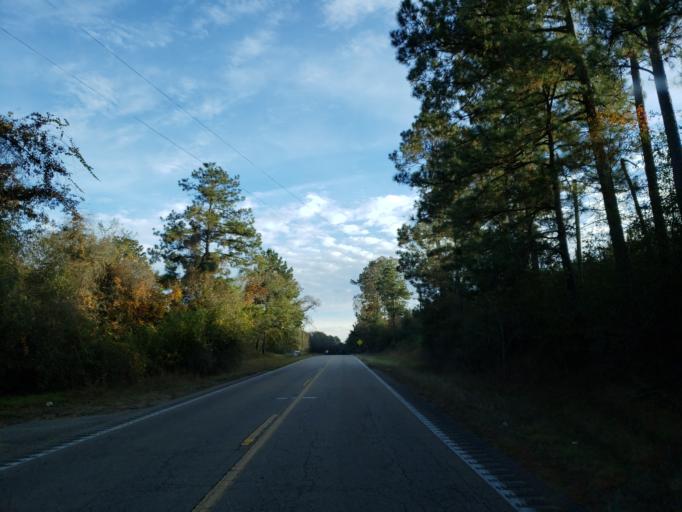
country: US
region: Mississippi
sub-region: Lamar County
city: Purvis
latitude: 31.1802
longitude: -89.4346
